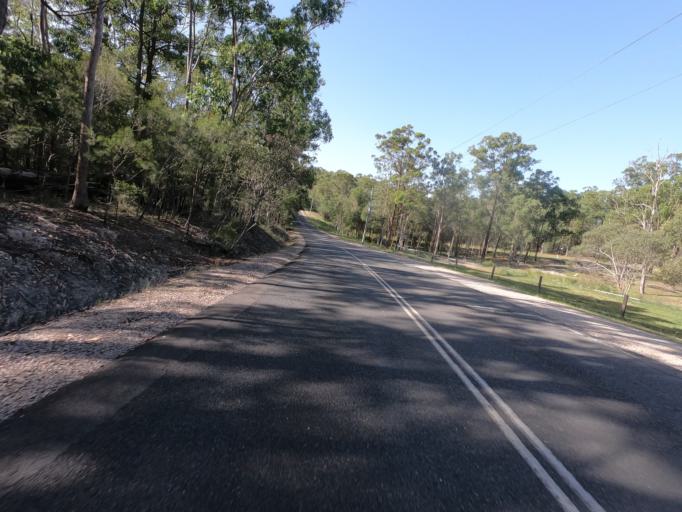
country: AU
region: Queensland
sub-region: Logan
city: Slacks Creek
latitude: -27.6085
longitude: 153.1842
